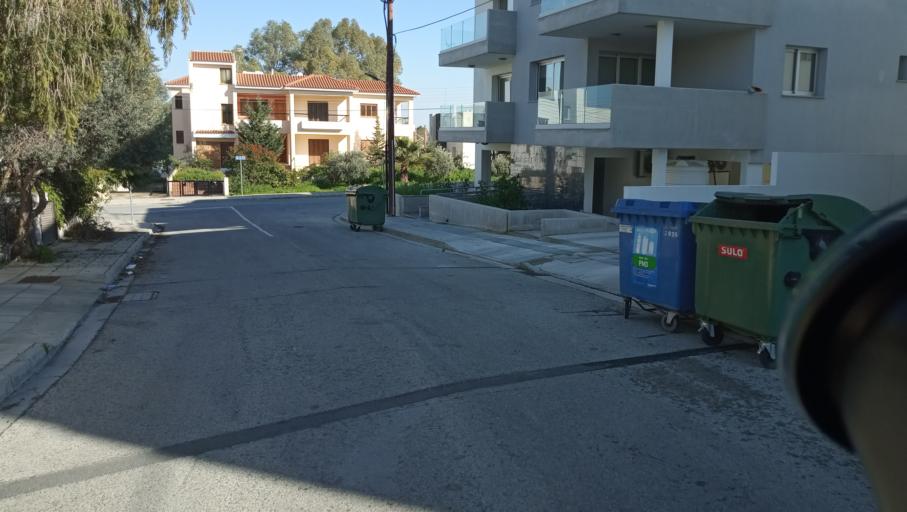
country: CY
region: Lefkosia
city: Nicosia
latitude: 35.1464
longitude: 33.3199
